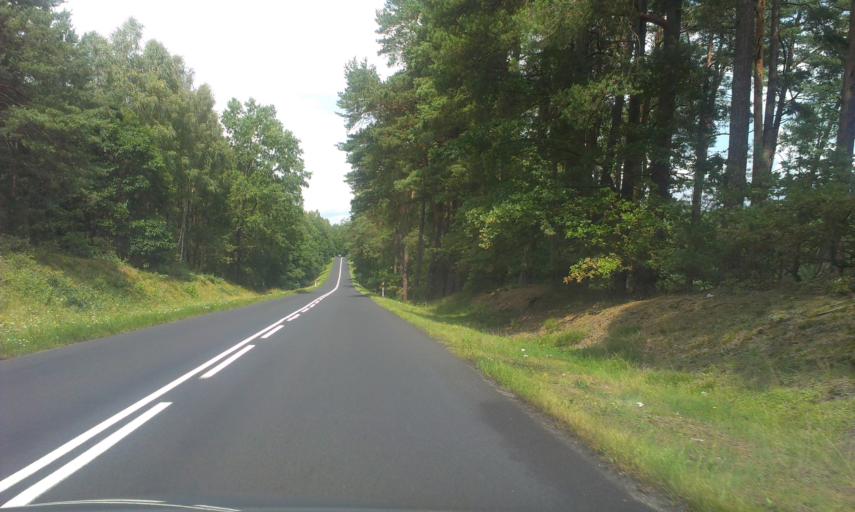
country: PL
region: West Pomeranian Voivodeship
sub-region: Powiat bialogardzki
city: Bialogard
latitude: 53.9407
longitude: 16.0603
